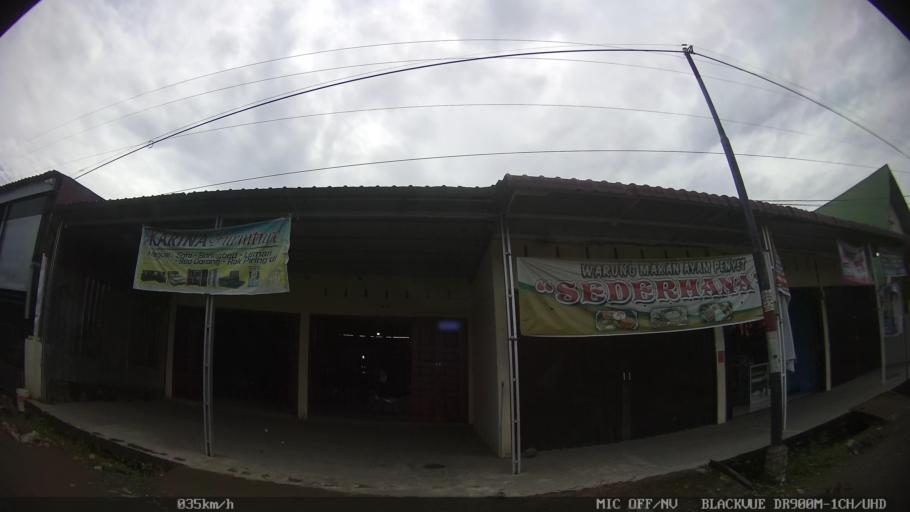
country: ID
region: North Sumatra
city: Sunggal
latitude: 3.5881
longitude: 98.5669
